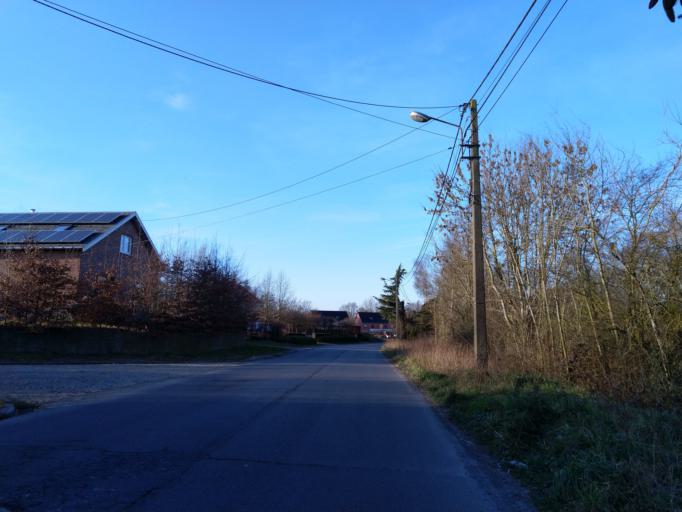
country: BE
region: Wallonia
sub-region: Province du Hainaut
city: Quevy-le-Petit
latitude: 50.3519
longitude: 3.8970
